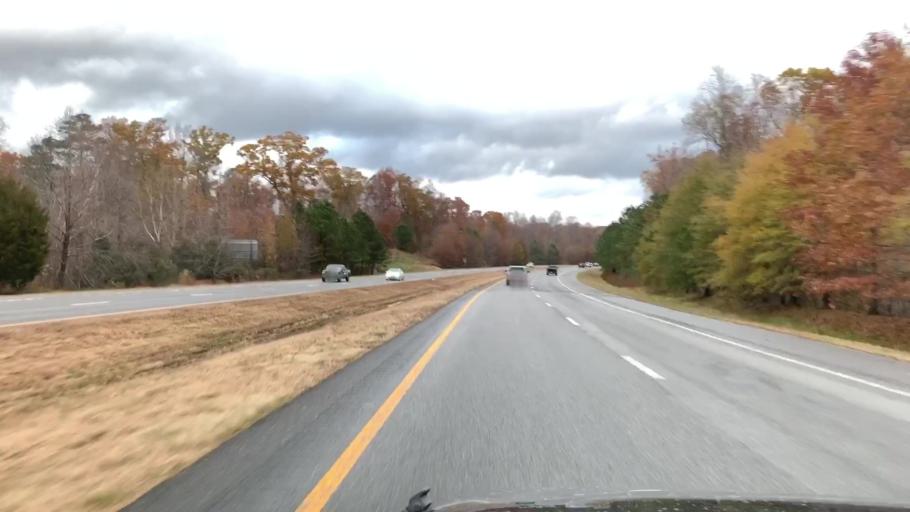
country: US
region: Virginia
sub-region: James City County
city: Williamsburg
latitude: 37.2914
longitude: -76.7521
